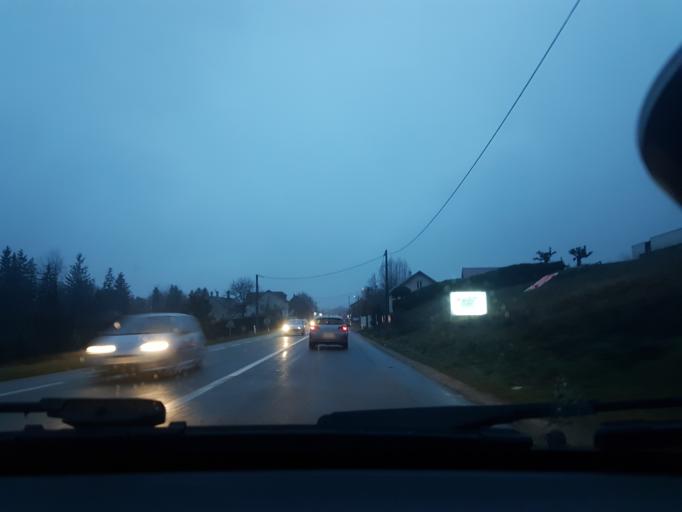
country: FR
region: Franche-Comte
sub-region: Departement du Doubs
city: Pontarlier
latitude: 46.8899
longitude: 6.3651
